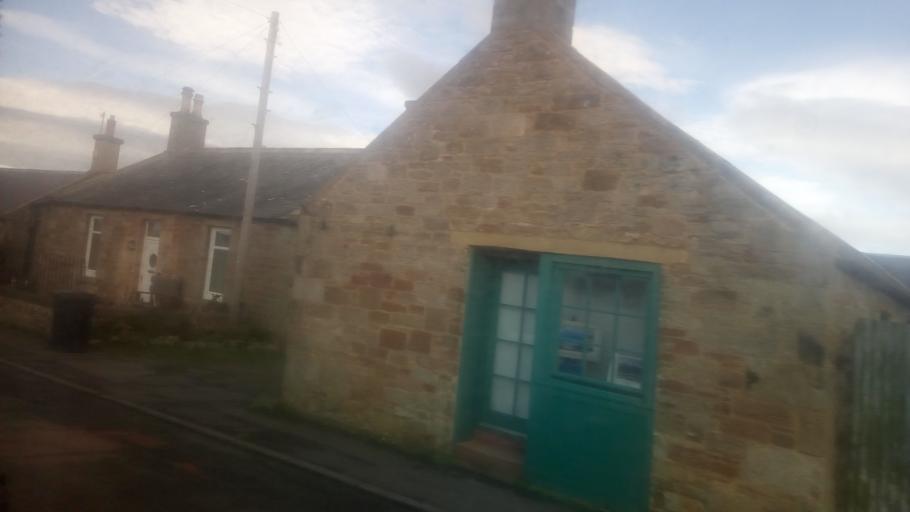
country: GB
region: Scotland
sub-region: Midlothian
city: Dalkeith
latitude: 55.8863
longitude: -3.0305
